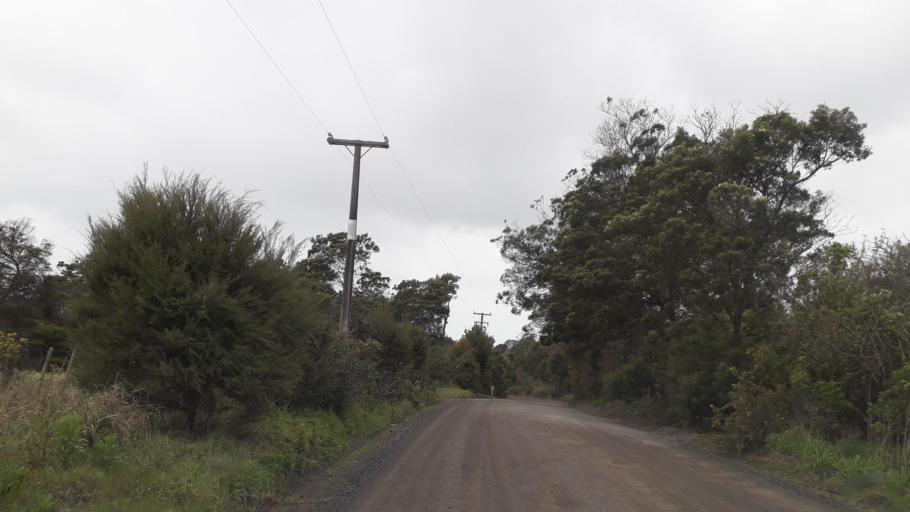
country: NZ
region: Northland
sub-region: Far North District
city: Kerikeri
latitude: -35.1401
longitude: 173.9989
